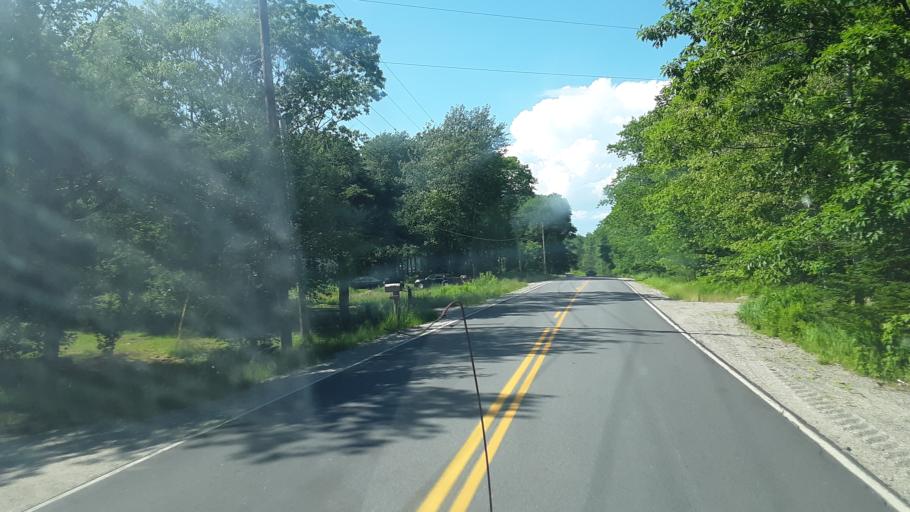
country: US
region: Maine
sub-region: Washington County
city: Cherryfield
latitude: 44.6342
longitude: -67.9419
